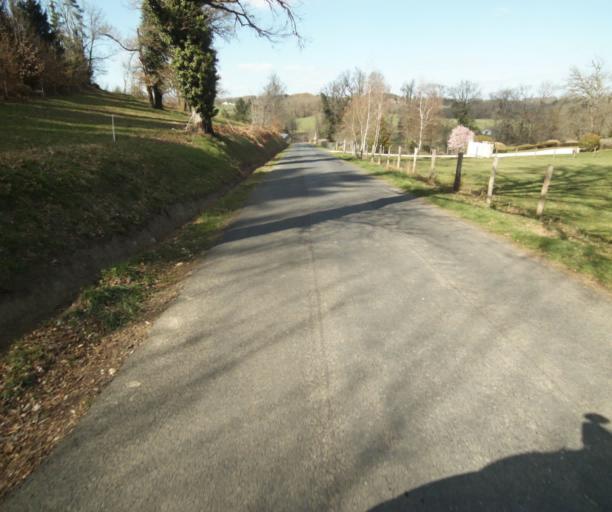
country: FR
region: Limousin
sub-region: Departement de la Correze
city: Saint-Mexant
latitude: 45.2908
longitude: 1.6172
